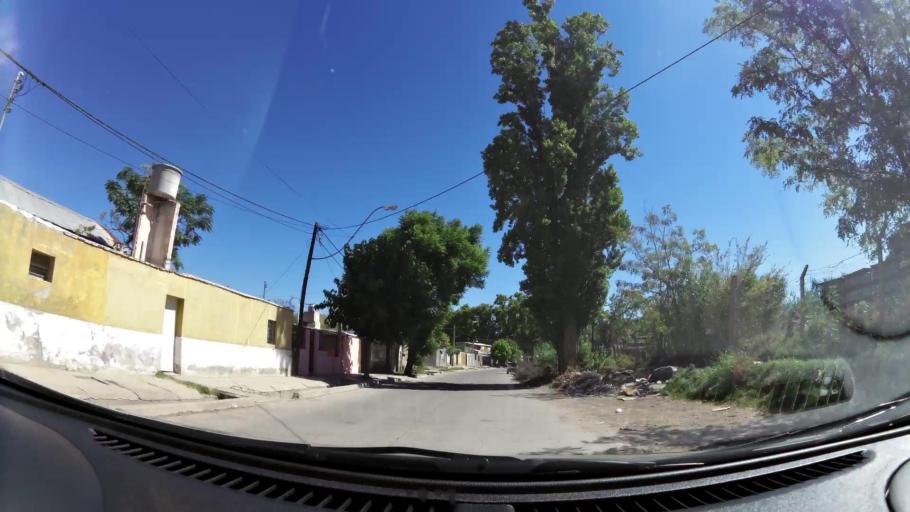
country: AR
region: Mendoza
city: Las Heras
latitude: -32.8328
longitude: -68.8415
